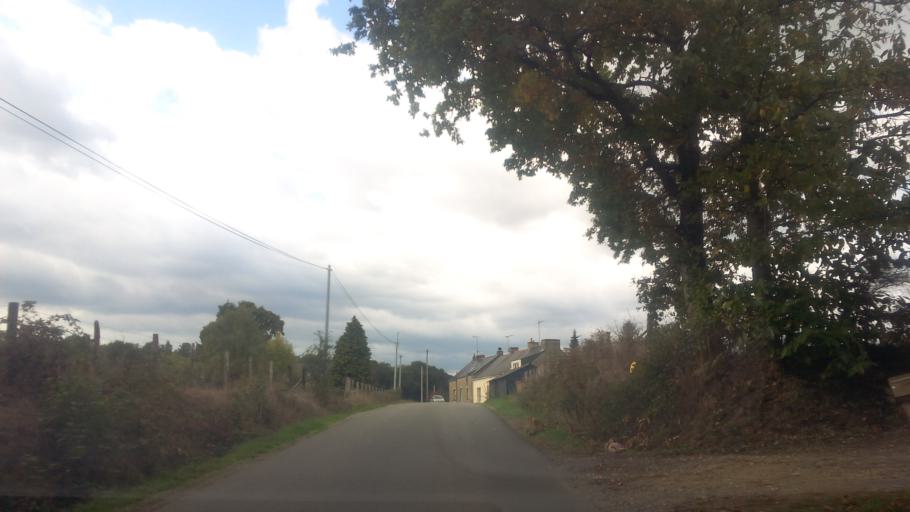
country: FR
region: Brittany
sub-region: Departement du Morbihan
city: Saint-Jean-la-Poterie
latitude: 47.6615
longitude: -2.1379
